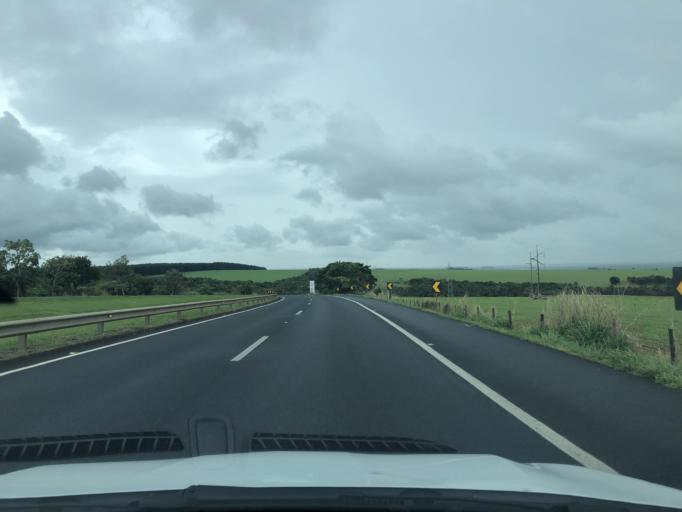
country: BR
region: Minas Gerais
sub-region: Uberlandia
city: Uberlandia
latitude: -19.0808
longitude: -48.1876
